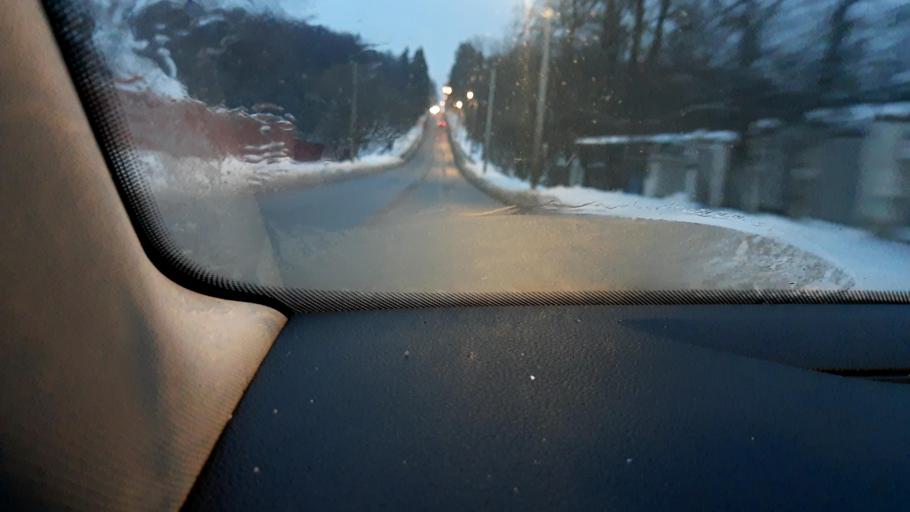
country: RU
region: Moskovskaya
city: Troitsk
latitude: 55.3160
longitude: 37.1546
